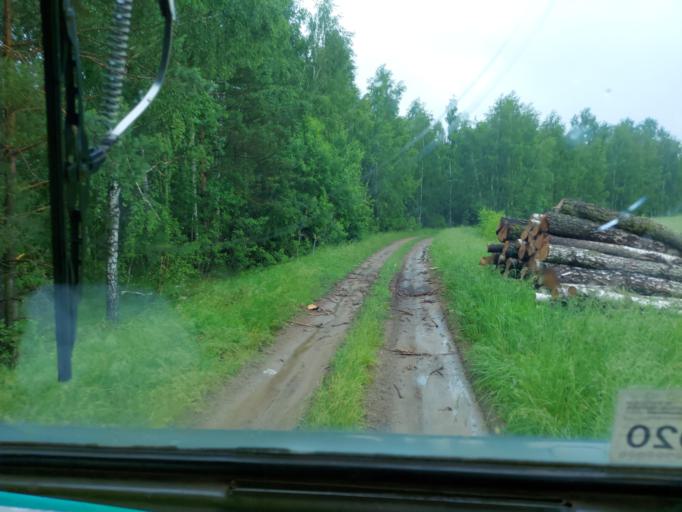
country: BY
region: Mogilev
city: Poselok Voskhod
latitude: 53.6735
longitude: 30.4027
